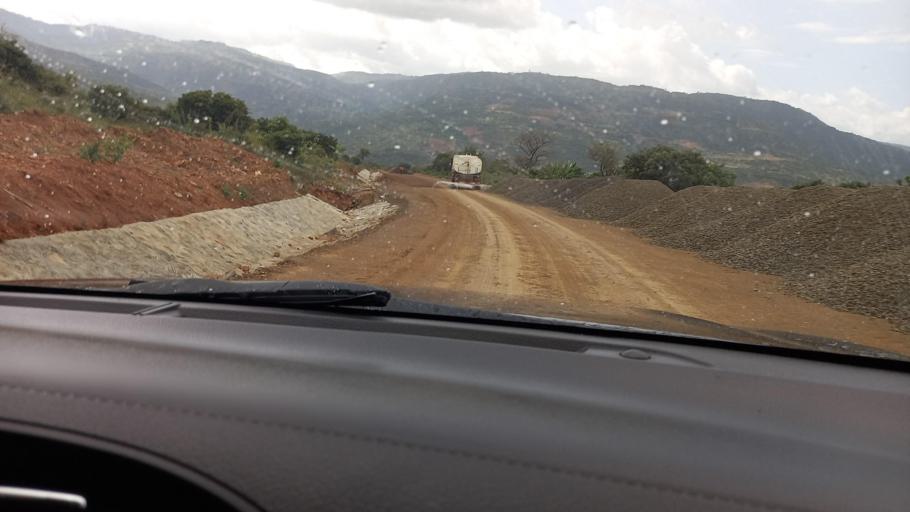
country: ET
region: Southern Nations, Nationalities, and People's Region
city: Mizan Teferi
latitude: 6.1866
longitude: 35.6907
